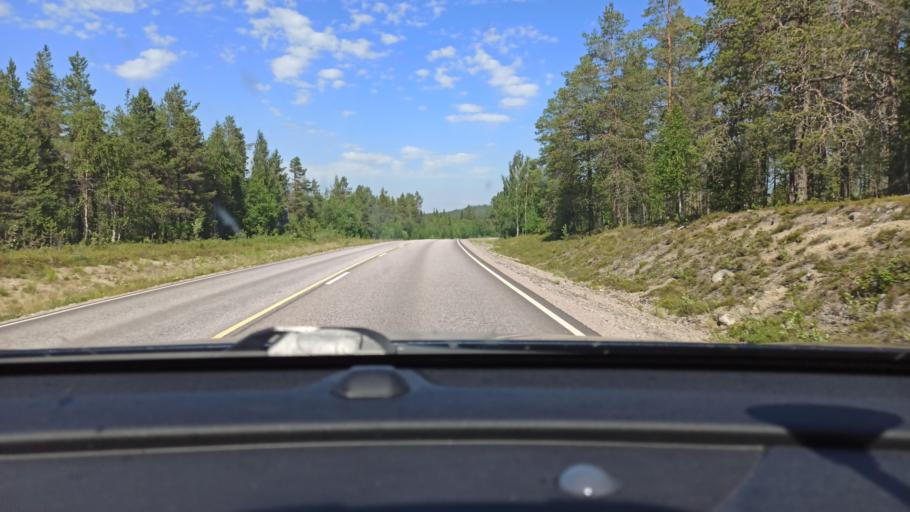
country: FI
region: Lapland
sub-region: Tunturi-Lappi
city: Muonio
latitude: 67.9974
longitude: 23.6150
